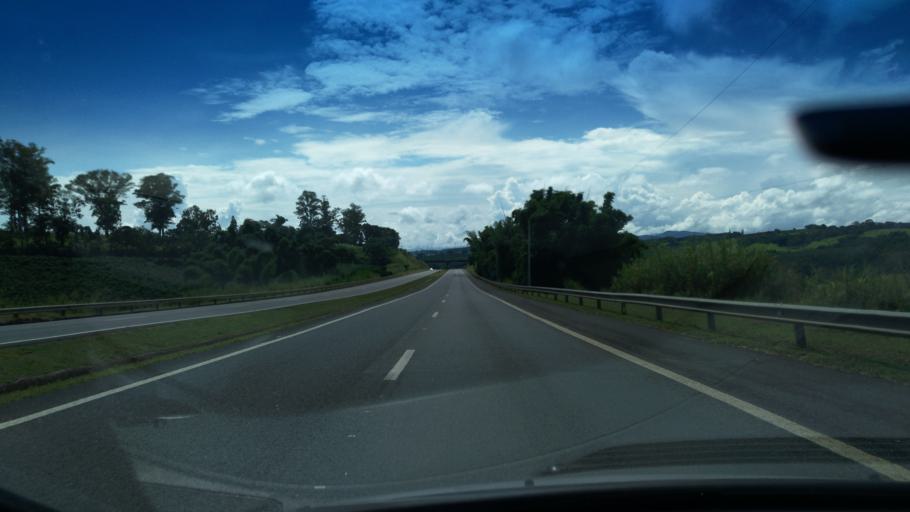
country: BR
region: Sao Paulo
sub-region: Santo Antonio Do Jardim
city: Espirito Santo do Pinhal
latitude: -22.2444
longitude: -46.8055
